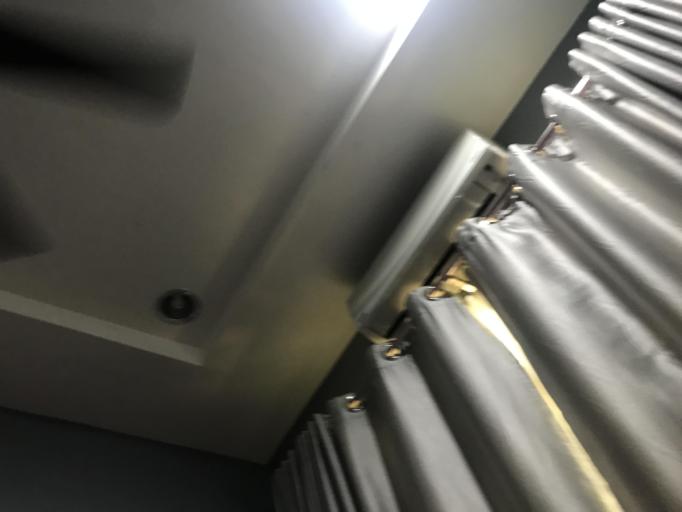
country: MY
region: Kelantan
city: Kota Bharu
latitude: 6.1128
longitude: 102.1818
